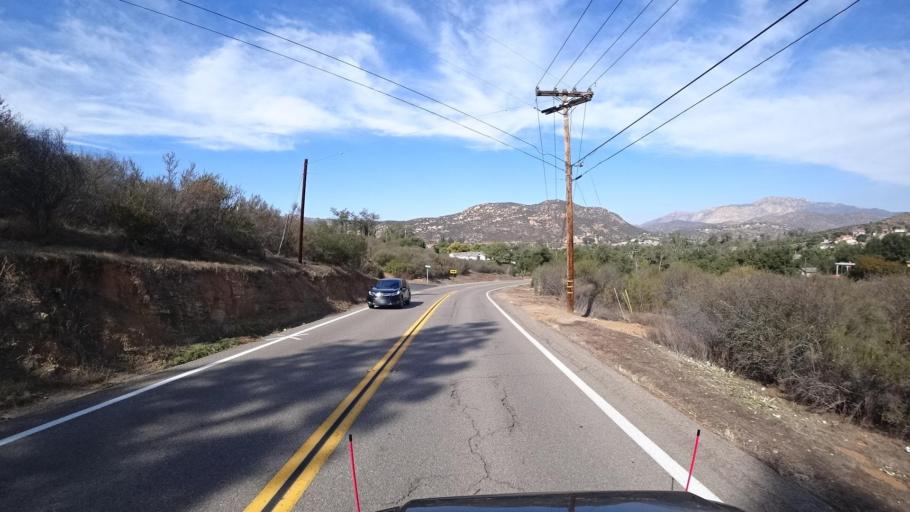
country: US
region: California
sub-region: San Diego County
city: Harbison Canyon
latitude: 32.8366
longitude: -116.8023
